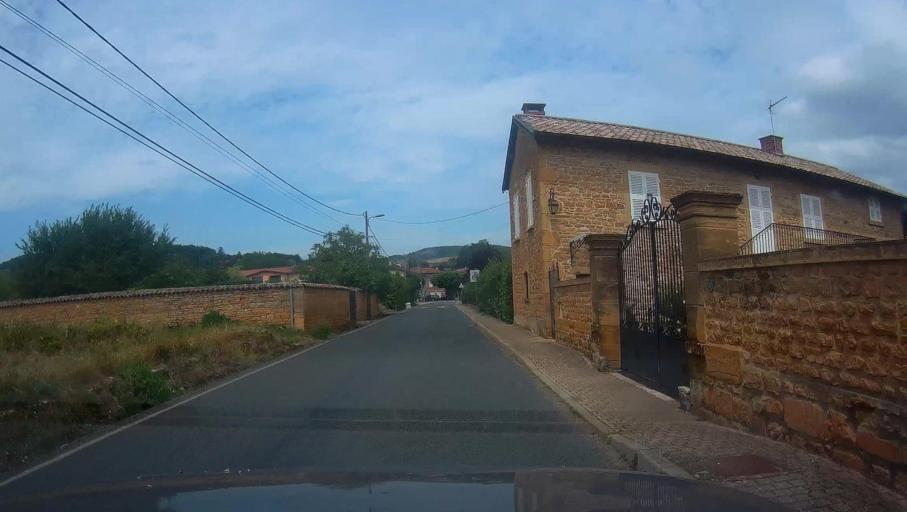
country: FR
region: Rhone-Alpes
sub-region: Departement du Rhone
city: Theize
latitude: 45.9230
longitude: 4.6189
